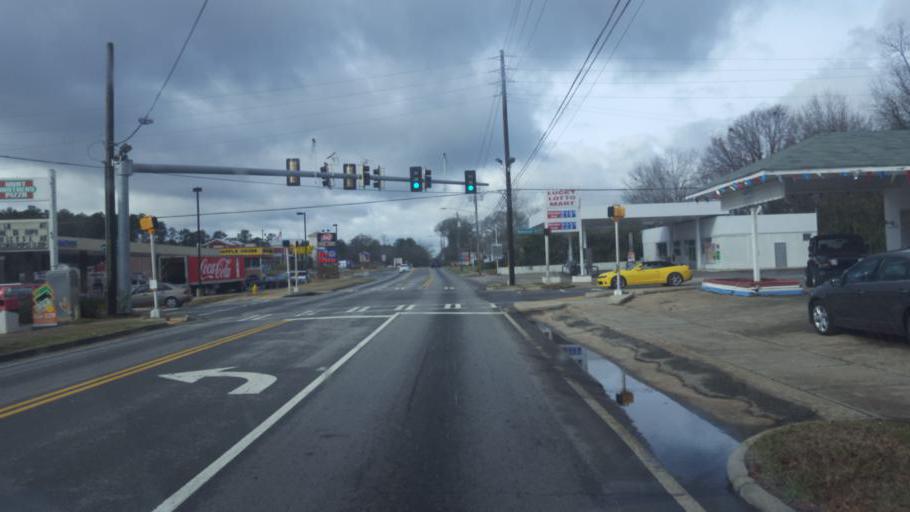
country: US
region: Georgia
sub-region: Butts County
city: Jackson
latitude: 33.2944
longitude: -83.9696
